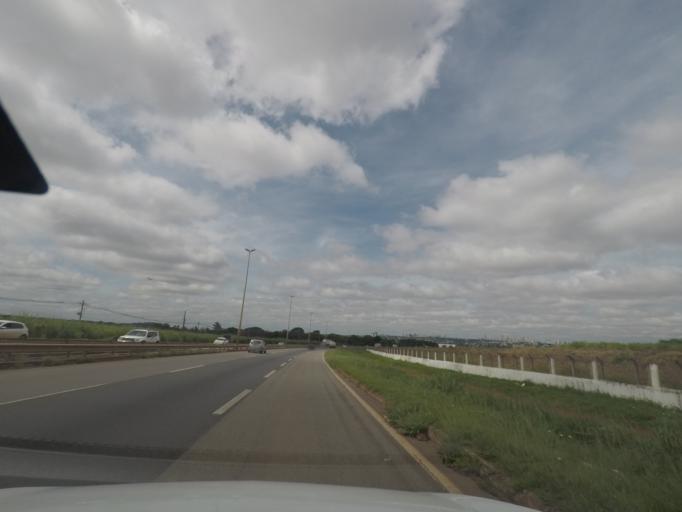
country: BR
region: Goias
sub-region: Goiania
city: Goiania
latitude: -16.6356
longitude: -49.2052
